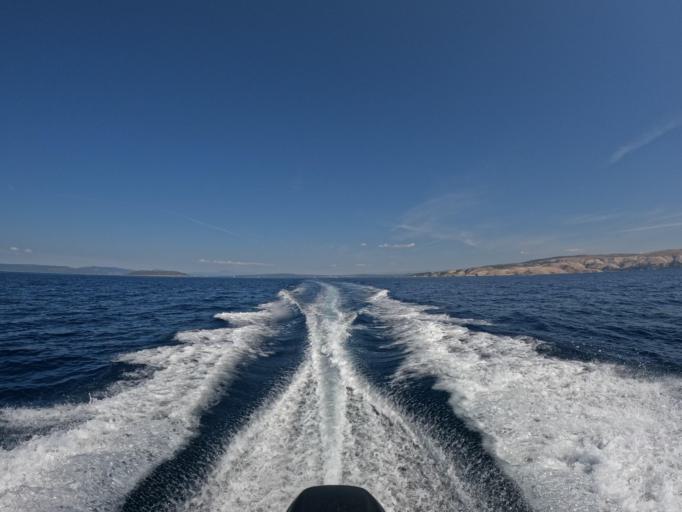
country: HR
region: Primorsko-Goranska
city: Punat
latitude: 44.9132
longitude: 14.6265
